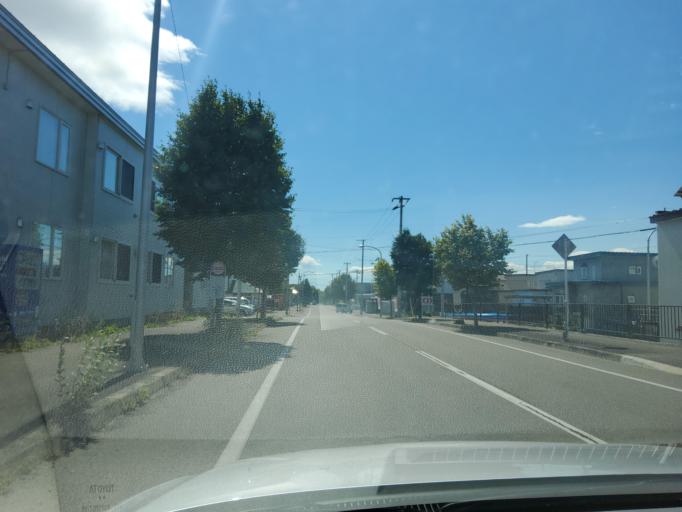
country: JP
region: Hokkaido
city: Obihiro
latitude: 42.9513
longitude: 143.1957
